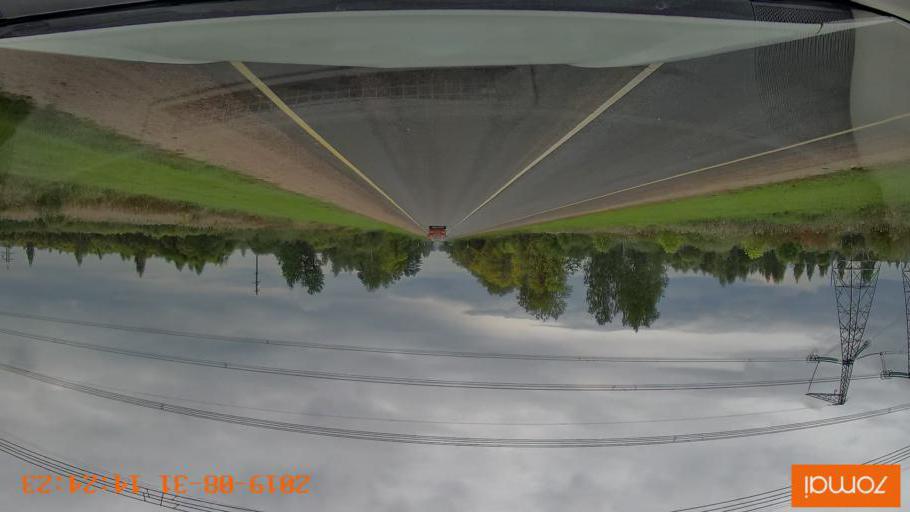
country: RU
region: Smolensk
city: Yekimovichi
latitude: 54.1026
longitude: 33.2542
